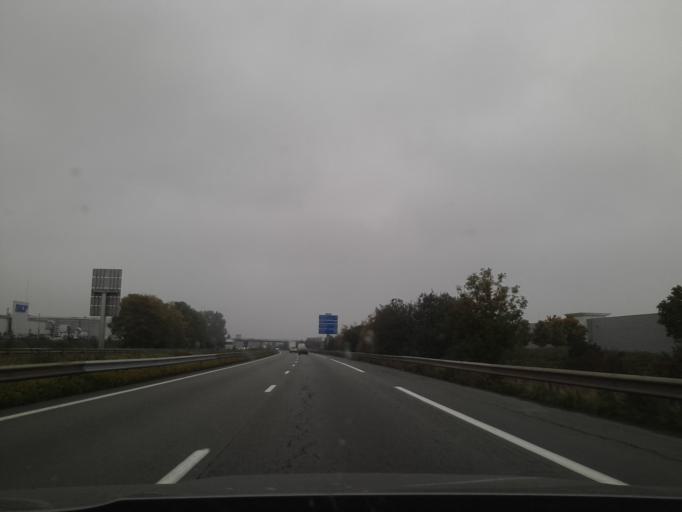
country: FR
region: Nord-Pas-de-Calais
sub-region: Departement du Nord
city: Prouvy
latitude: 50.3361
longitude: 3.4508
